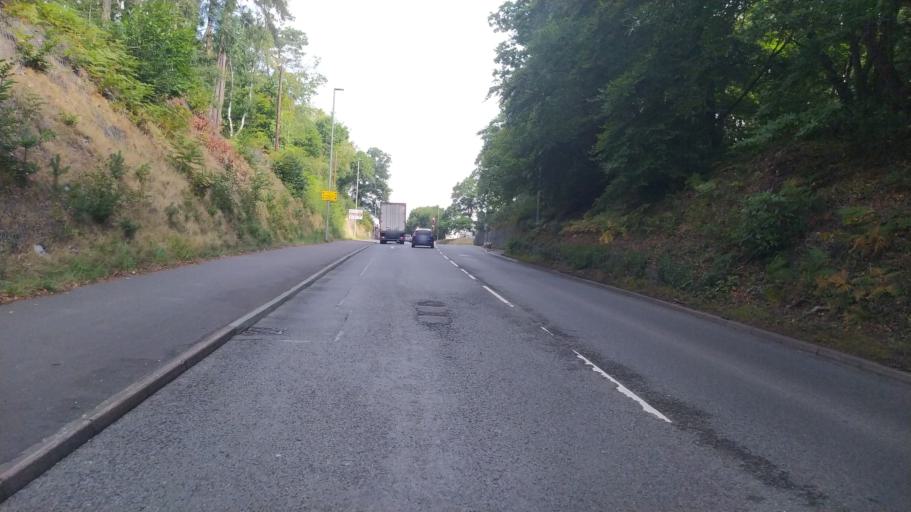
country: GB
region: England
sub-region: Dorset
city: Wimborne Minster
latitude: 50.7766
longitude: -1.9780
